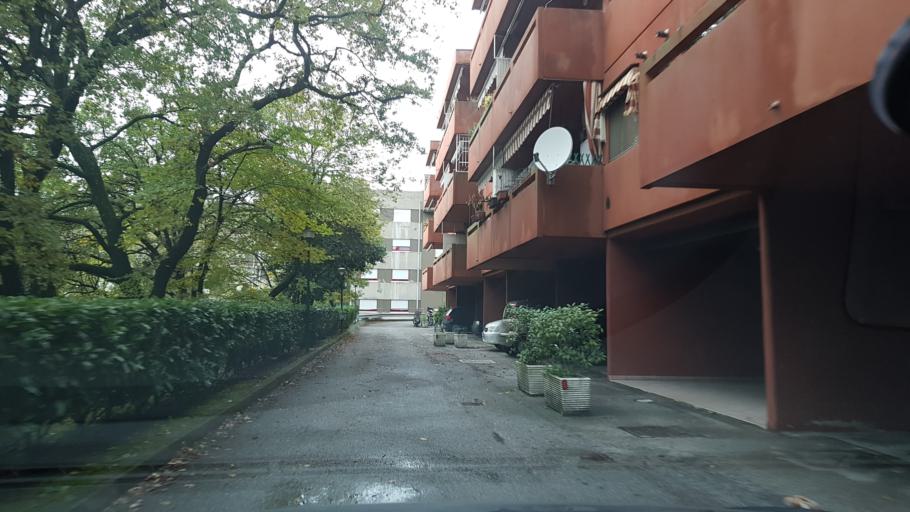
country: IT
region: Friuli Venezia Giulia
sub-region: Provincia di Trieste
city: Domio
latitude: 45.6386
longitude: 13.8229
